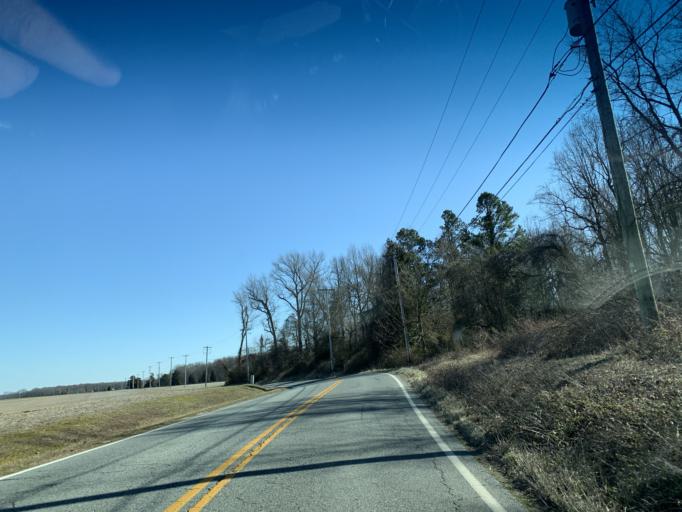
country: US
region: Maryland
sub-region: Cecil County
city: North East
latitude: 39.4931
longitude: -75.8810
